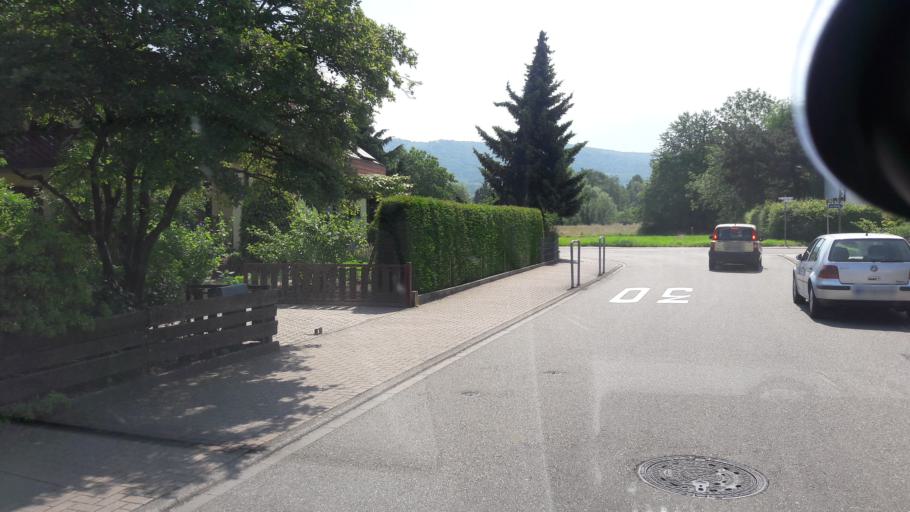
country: DE
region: Baden-Wuerttemberg
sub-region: Karlsruhe Region
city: Malsch
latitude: 48.8861
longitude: 8.3272
